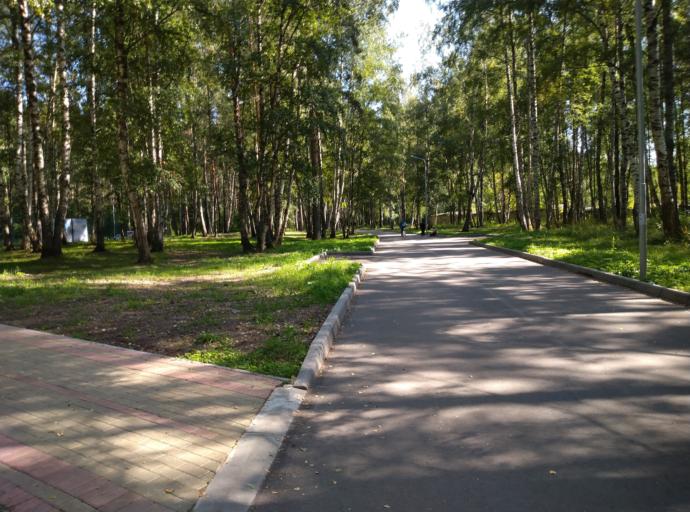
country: RU
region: Kostroma
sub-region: Kostromskoy Rayon
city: Kostroma
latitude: 57.7937
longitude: 40.9640
